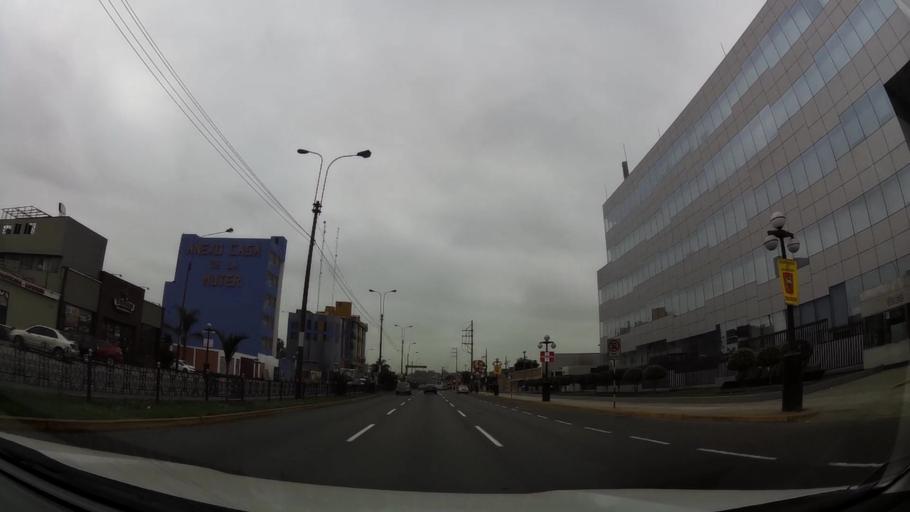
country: PE
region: Lima
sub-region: Lima
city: Surco
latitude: -12.1790
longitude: -77.0147
